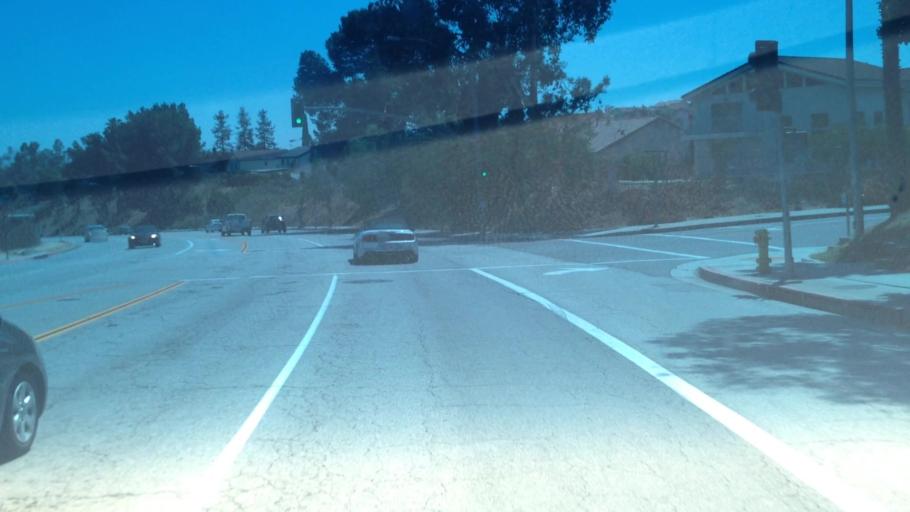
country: US
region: California
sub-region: Los Angeles County
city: Montebello
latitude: 34.0300
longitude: -118.1011
